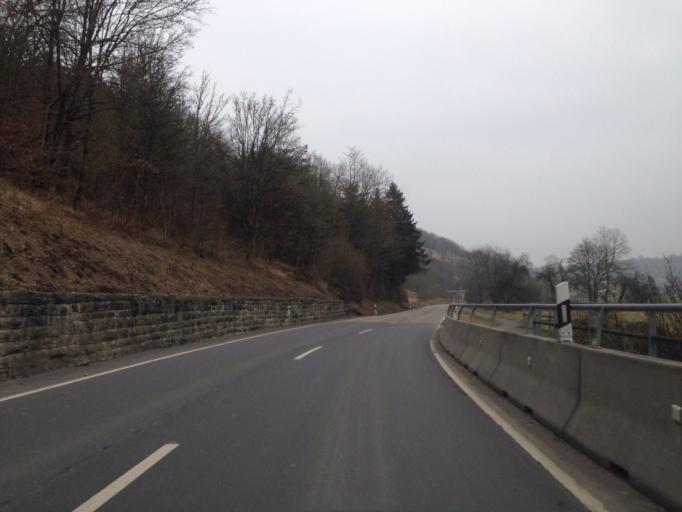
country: DE
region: Baden-Wuerttemberg
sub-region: Regierungsbezirk Stuttgart
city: Jagsthausen
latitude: 49.3313
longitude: 9.4865
